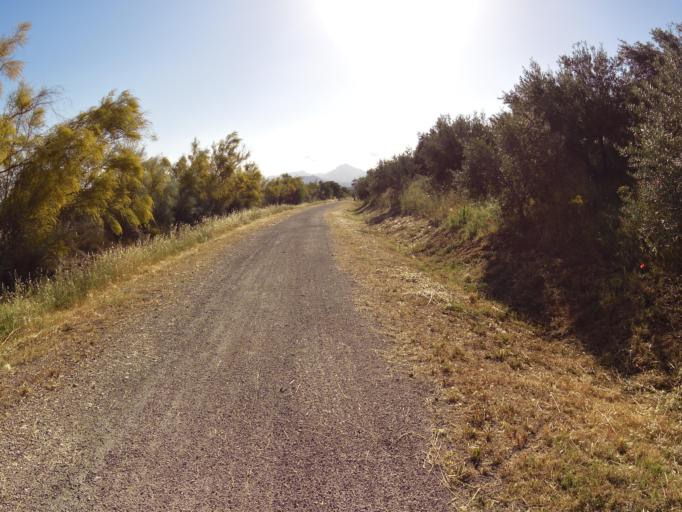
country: ES
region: Andalusia
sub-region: Province of Cordoba
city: Luque
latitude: 37.5717
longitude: -4.2300
